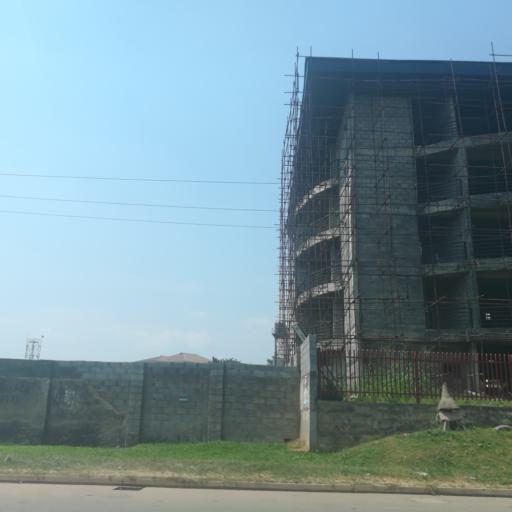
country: NG
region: Abuja Federal Capital Territory
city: Abuja
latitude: 9.0673
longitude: 7.4331
